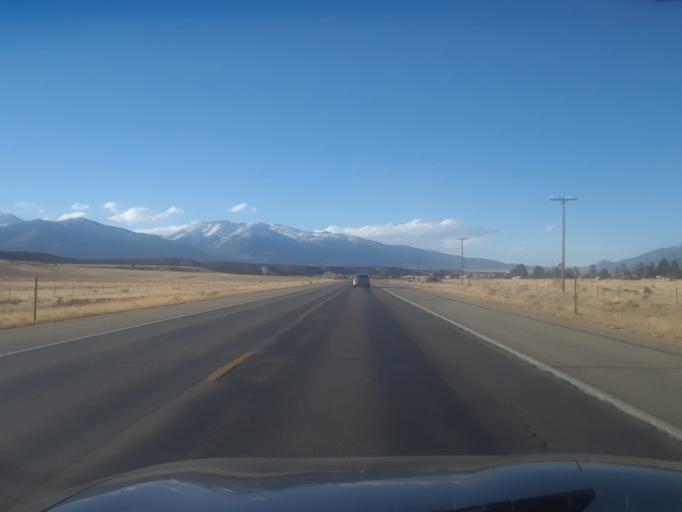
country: US
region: Colorado
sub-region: Chaffee County
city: Buena Vista
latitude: 38.7569
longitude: -106.0849
